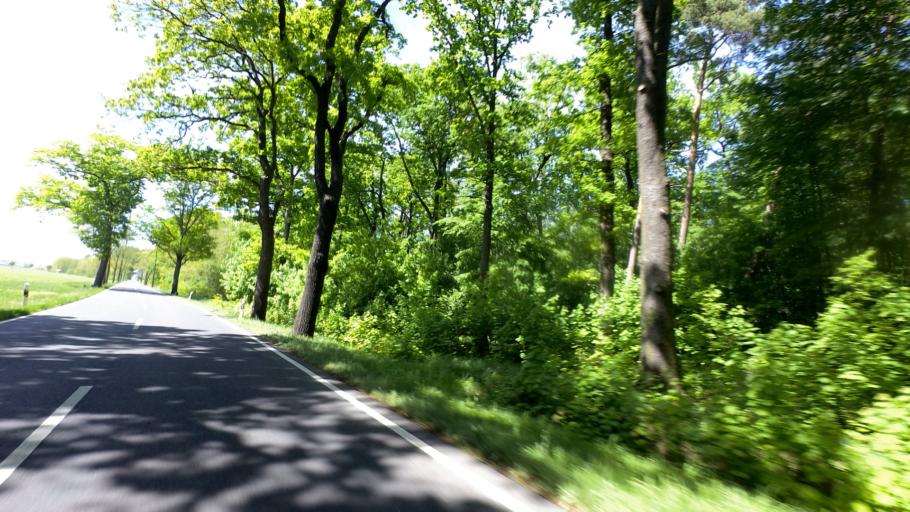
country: DE
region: Brandenburg
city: Sperenberg
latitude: 52.0840
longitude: 13.4220
